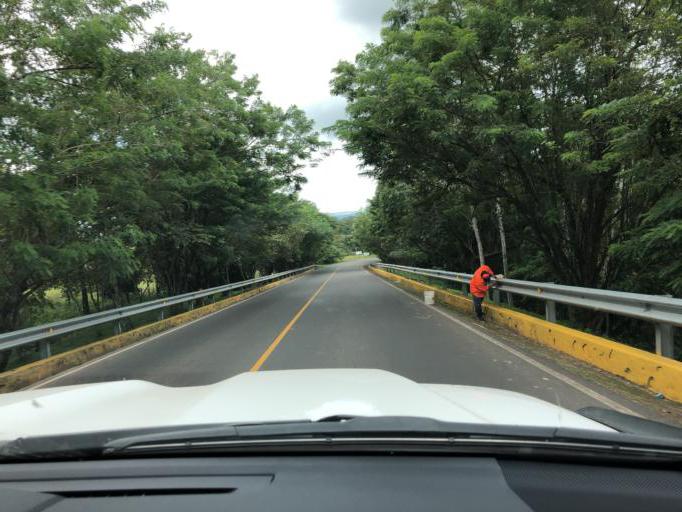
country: NI
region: Chontales
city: Santo Tomas
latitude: 12.0604
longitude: -85.0574
